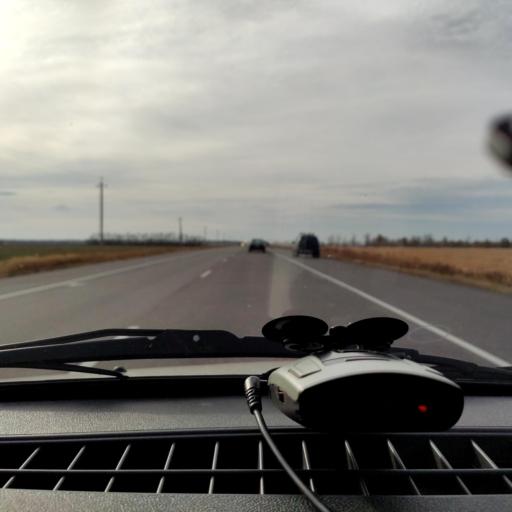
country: RU
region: Voronezj
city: Devitsa
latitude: 51.5662
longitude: 38.9738
